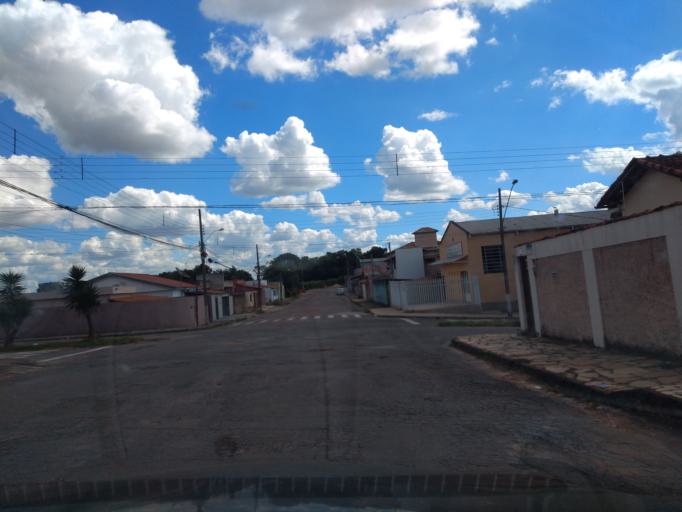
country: BR
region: Minas Gerais
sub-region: Tres Coracoes
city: Tres Coracoes
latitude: -21.6834
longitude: -45.2694
